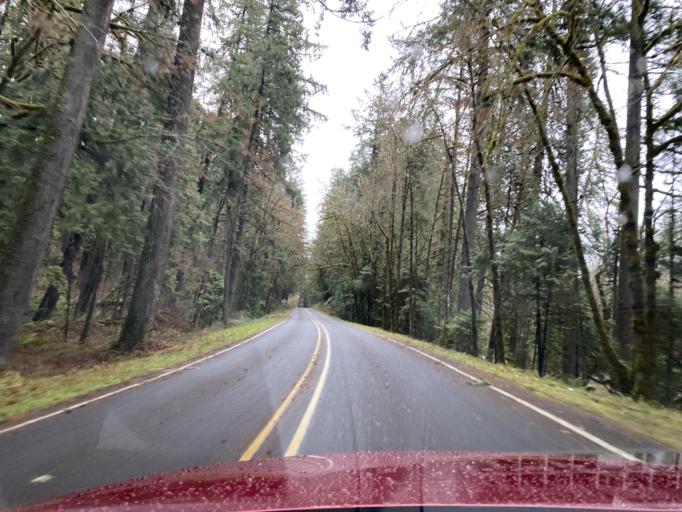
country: US
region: Oregon
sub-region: Lane County
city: Oakridge
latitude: 43.7487
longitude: -122.5236
